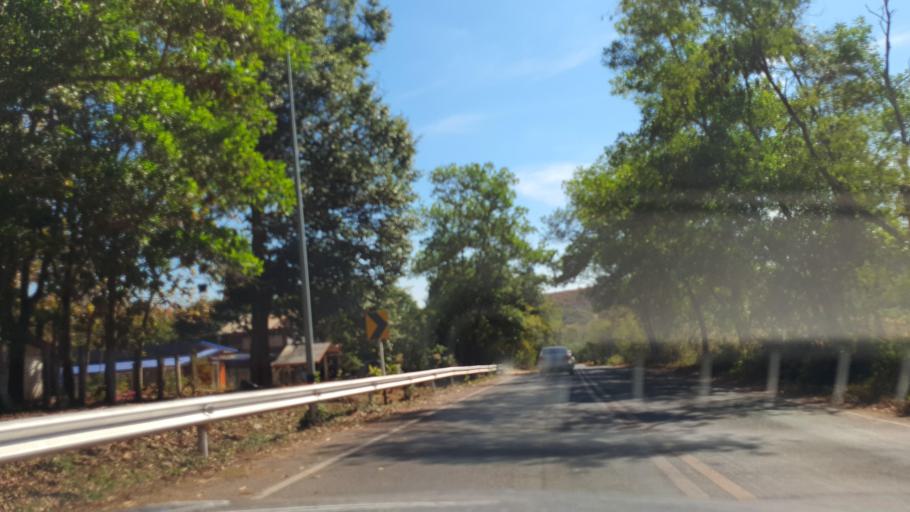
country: TH
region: Kalasin
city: Khao Wong
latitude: 16.7818
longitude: 104.1510
